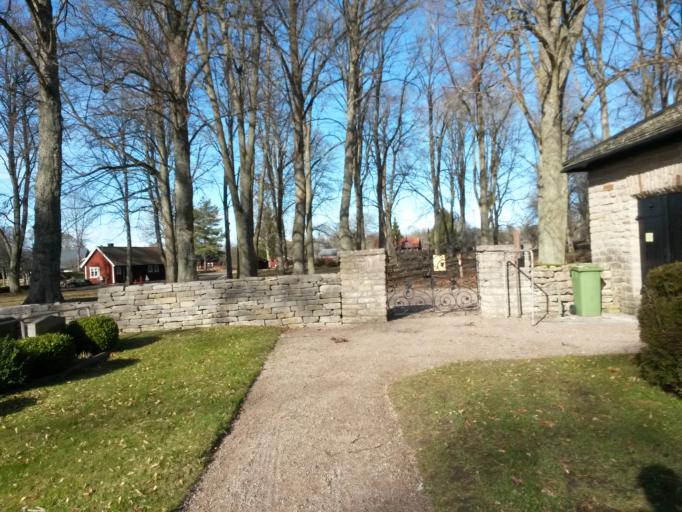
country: SE
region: Vaestra Goetaland
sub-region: Skara Kommun
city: Axvall
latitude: 58.3848
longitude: 13.6560
